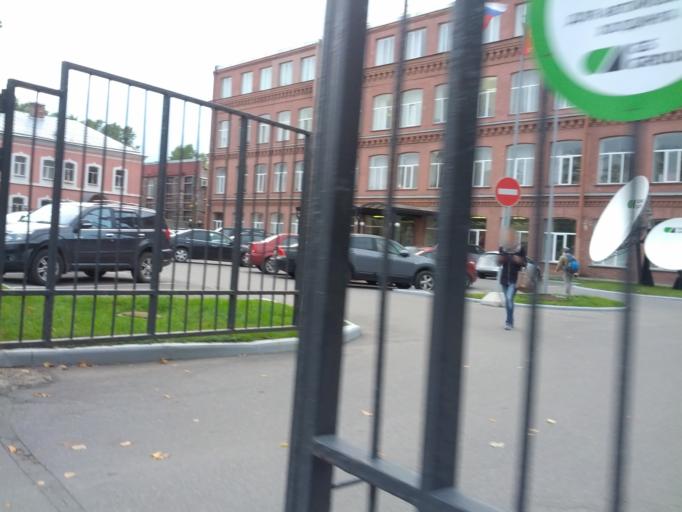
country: RU
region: Leningrad
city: Krestovskiy ostrov
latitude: 59.9620
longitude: 30.2732
